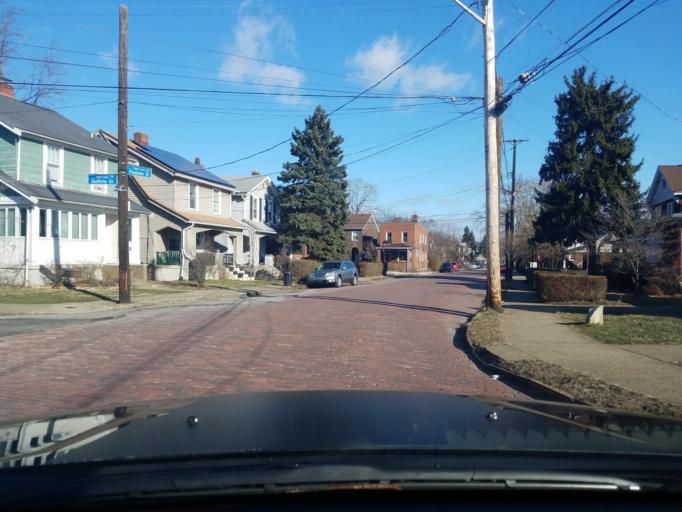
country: US
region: Pennsylvania
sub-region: Allegheny County
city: Wilkinsburg
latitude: 40.4387
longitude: -79.8949
